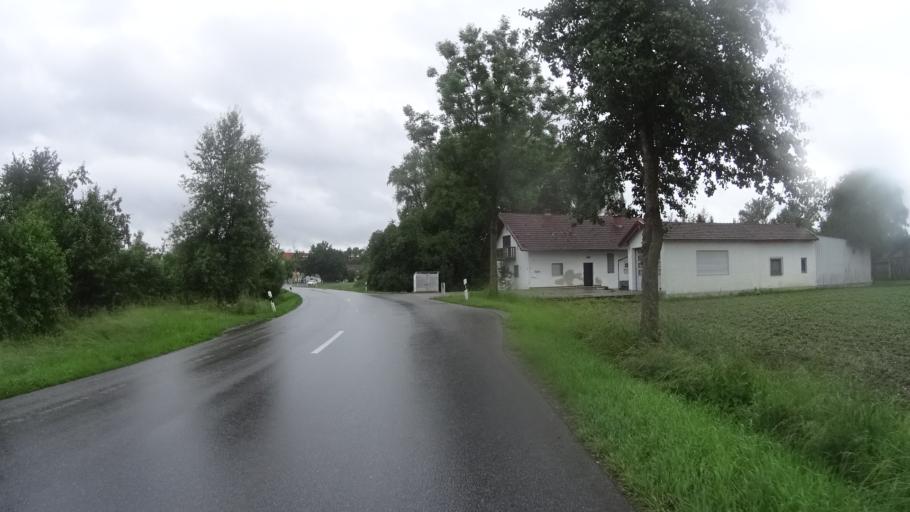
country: AT
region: Upper Austria
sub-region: Politischer Bezirk Scharding
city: Scharding
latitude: 48.4426
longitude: 13.4006
